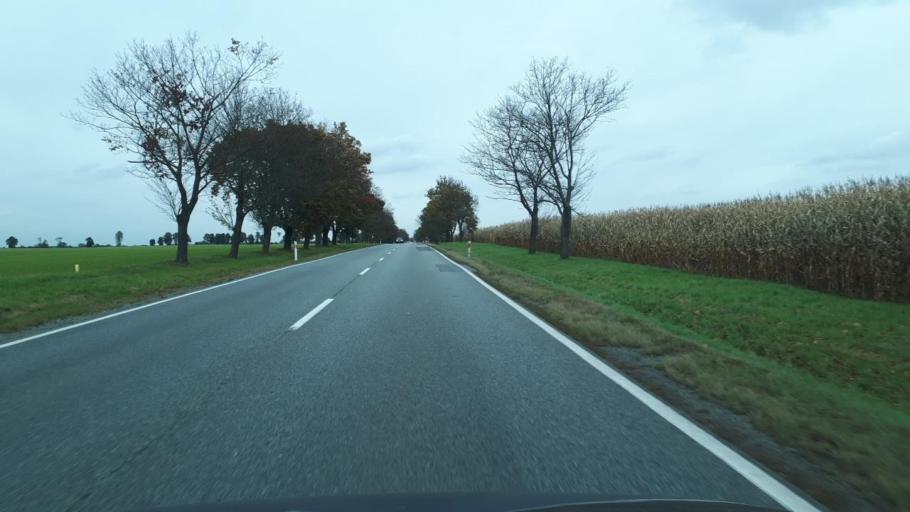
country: PL
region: Opole Voivodeship
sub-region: Powiat kluczborski
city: Byczyna
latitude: 51.0877
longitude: 18.1996
